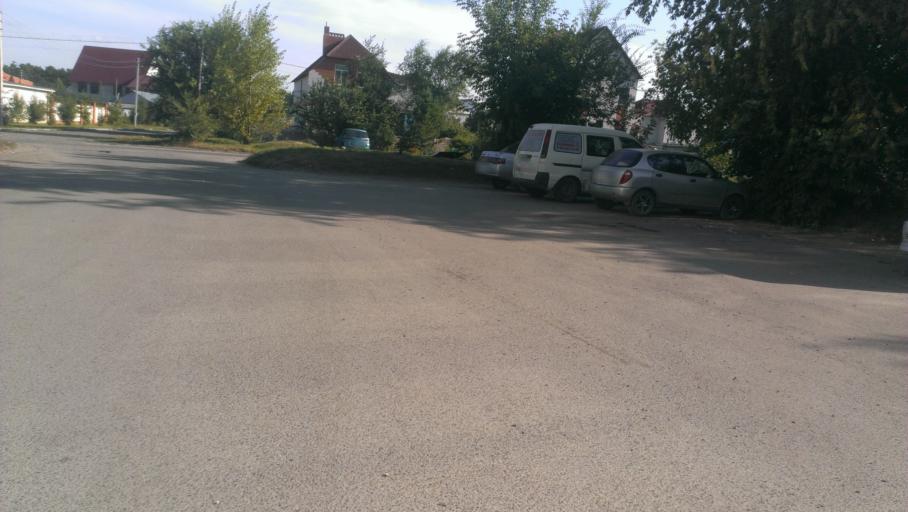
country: RU
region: Altai Krai
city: Novosilikatnyy
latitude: 53.3050
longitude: 83.6240
